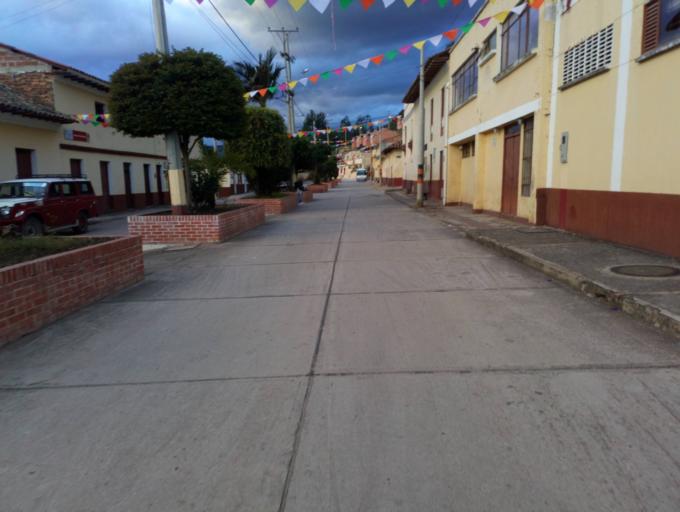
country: CO
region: Boyaca
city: Susacon
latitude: 6.1308
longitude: -72.7086
